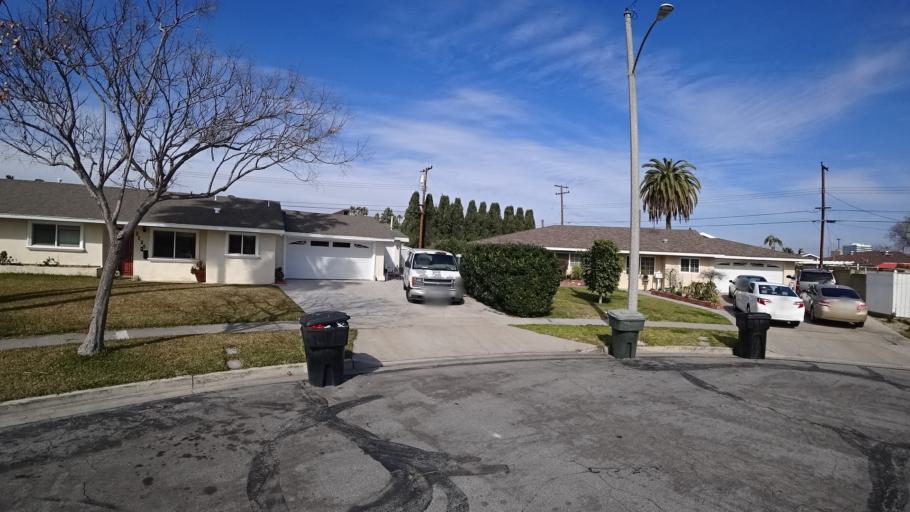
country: US
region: California
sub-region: Orange County
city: Anaheim
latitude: 33.7950
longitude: -117.9014
